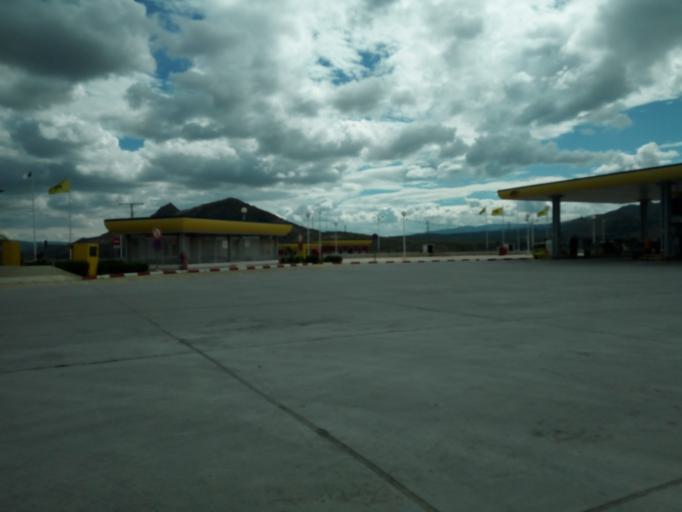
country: DZ
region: Bordj Bou Arreridj
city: Mansourah
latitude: 36.2023
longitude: 4.4003
